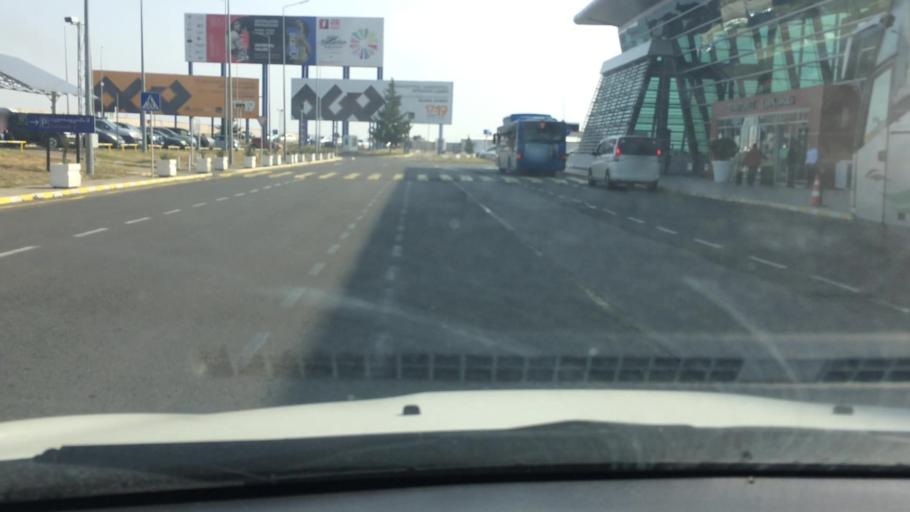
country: GE
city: Didi Lilo
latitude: 41.6699
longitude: 44.9650
